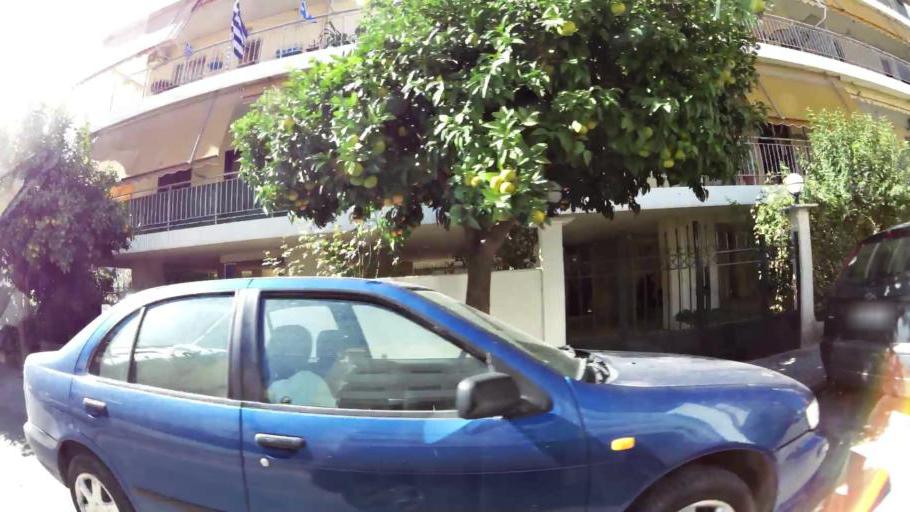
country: GR
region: Attica
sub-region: Nomarchia Athinas
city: Khalandrion
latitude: 38.0343
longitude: 23.7990
